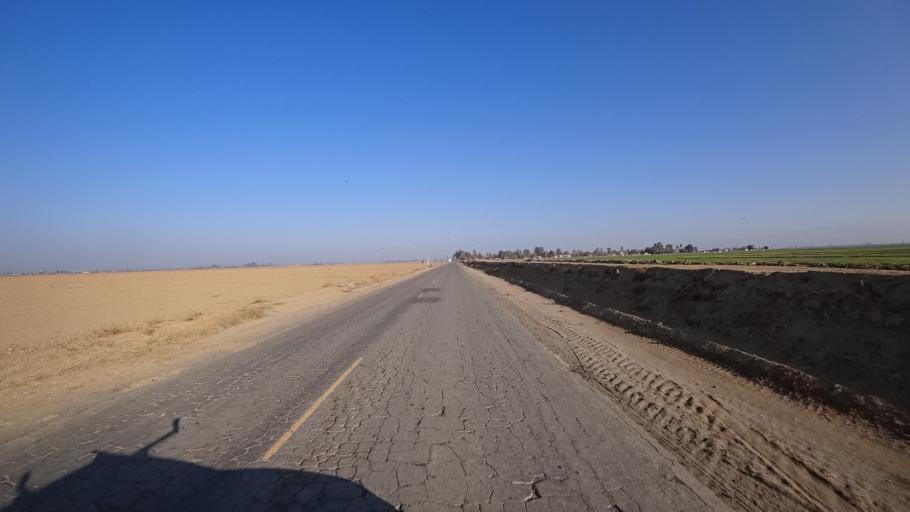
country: US
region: California
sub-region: Kern County
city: Greenfield
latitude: 35.2332
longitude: -118.9677
